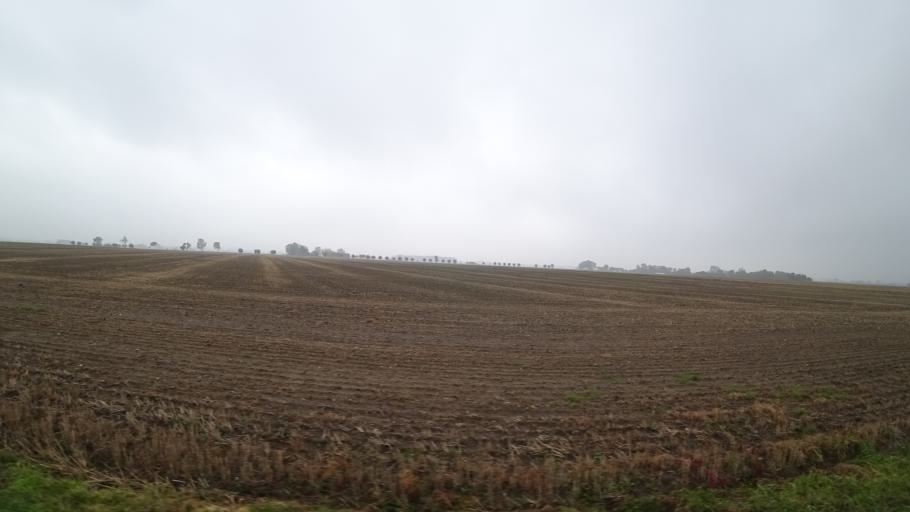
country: SE
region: Skane
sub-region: Kavlinge Kommun
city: Kaevlinge
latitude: 55.8112
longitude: 13.1429
